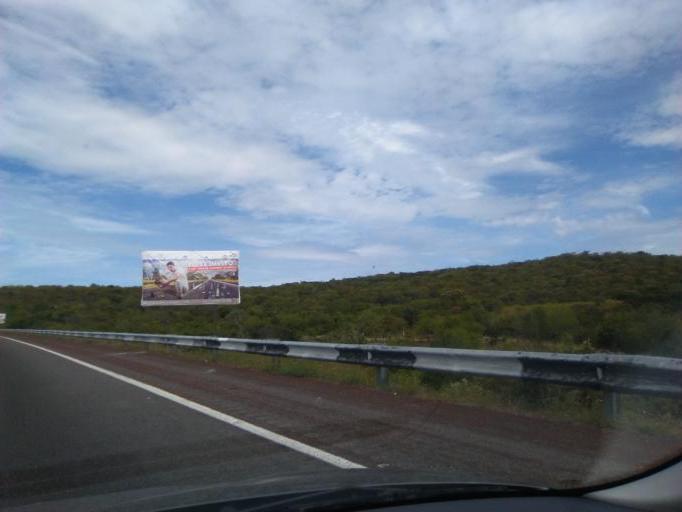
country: MX
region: Guerrero
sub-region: Eduardo Neri
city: Axaxacualco
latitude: 17.8095
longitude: -99.4648
